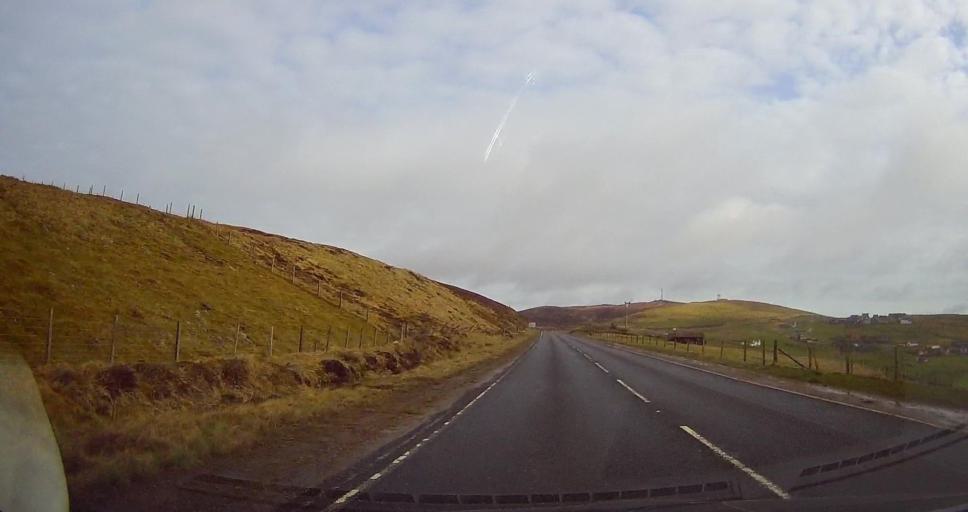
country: GB
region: Scotland
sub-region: Shetland Islands
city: Lerwick
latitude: 60.1307
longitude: -1.2151
